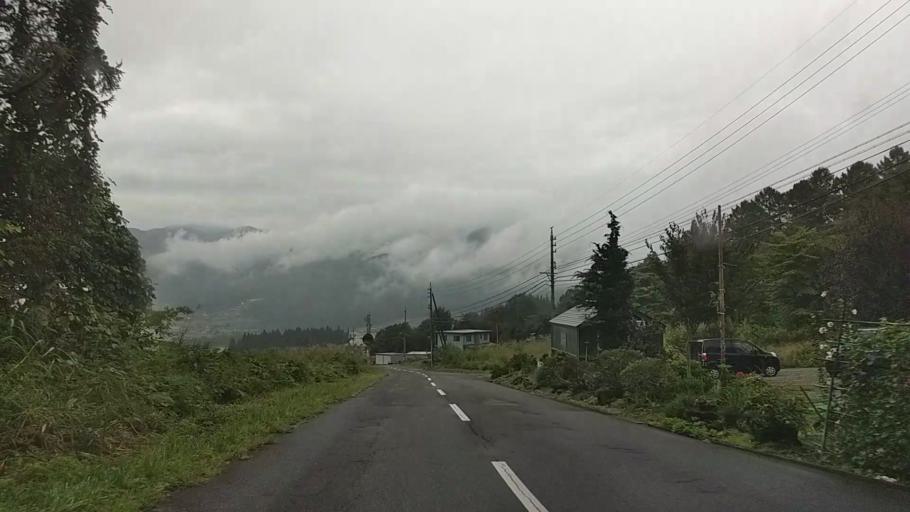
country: JP
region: Nagano
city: Iiyama
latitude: 36.8262
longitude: 138.3980
